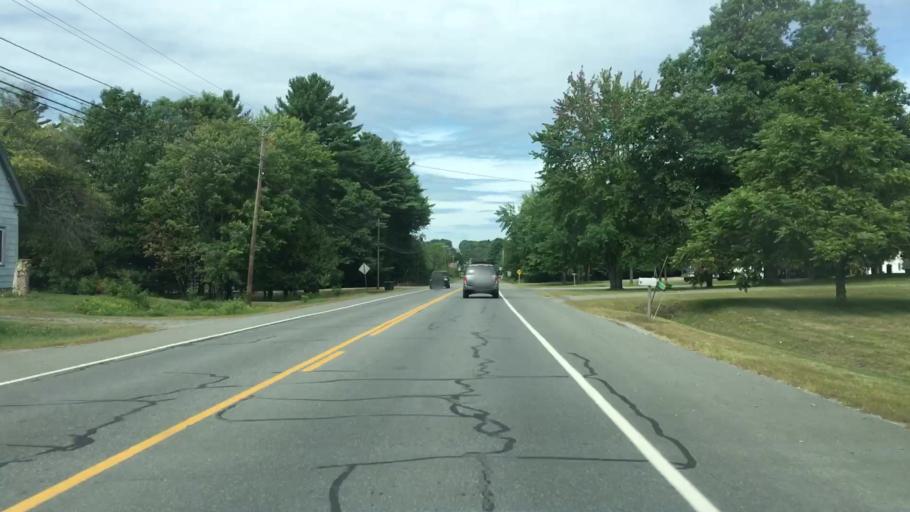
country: US
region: Maine
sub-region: Piscataquis County
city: Milo
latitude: 45.2673
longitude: -68.9951
